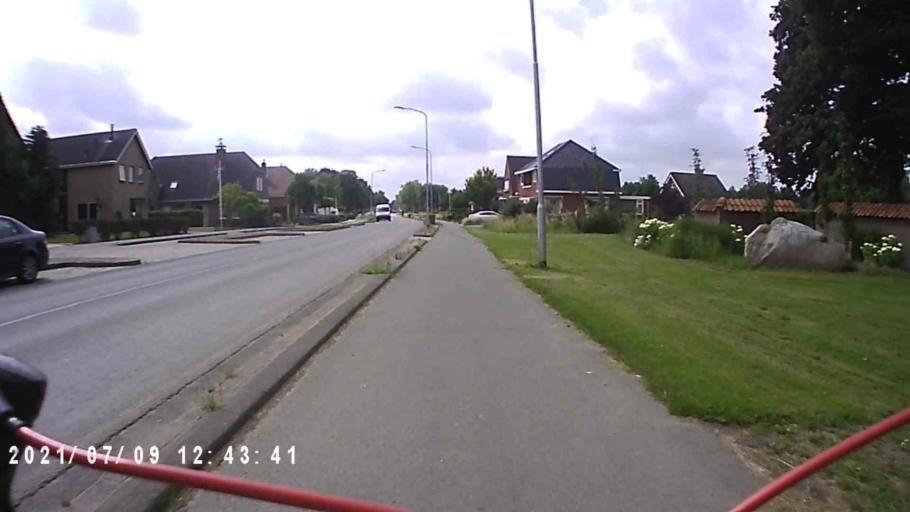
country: NL
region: Groningen
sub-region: Gemeente  Oldambt
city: Winschoten
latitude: 53.1354
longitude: 7.0227
